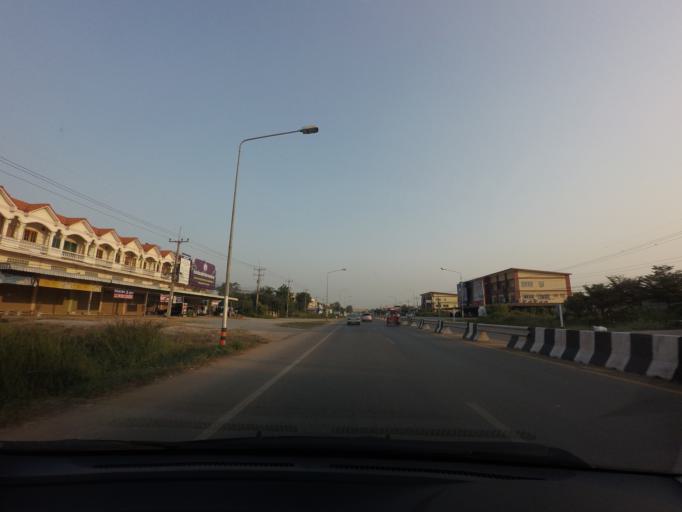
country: TH
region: Sukhothai
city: Sukhothai
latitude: 17.0185
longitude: 99.8297
